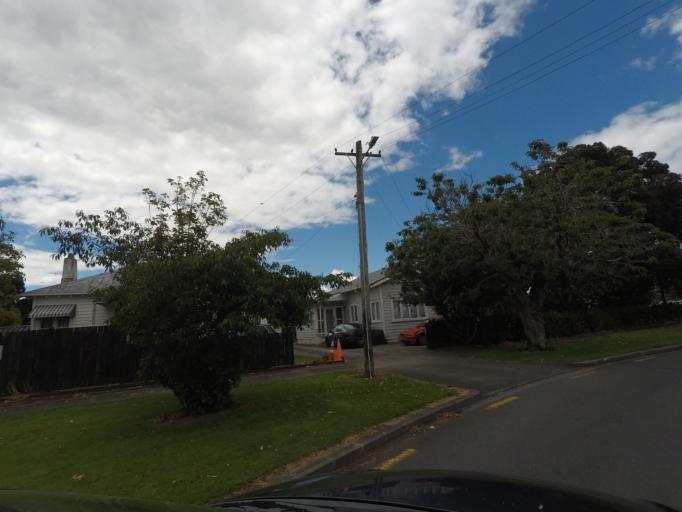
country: NZ
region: Auckland
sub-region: Auckland
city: Auckland
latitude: -36.8811
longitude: 174.7343
